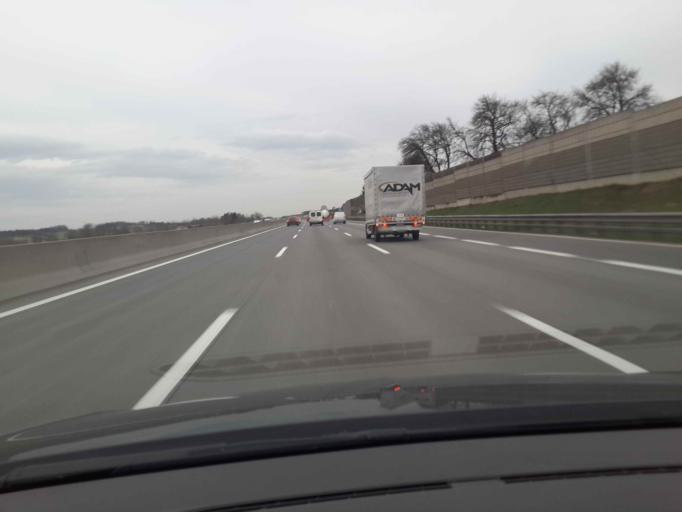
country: AT
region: Lower Austria
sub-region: Politischer Bezirk Amstetten
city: Amstetten
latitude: 48.1461
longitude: 14.8702
